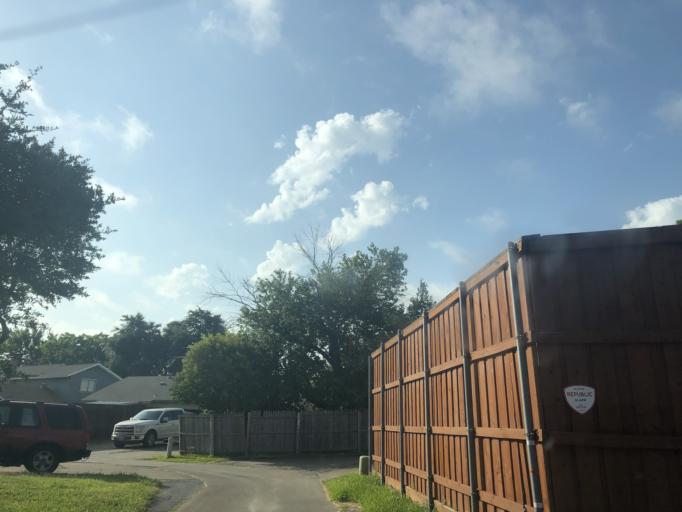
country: US
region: Texas
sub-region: Dallas County
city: Garland
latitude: 32.8517
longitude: -96.6299
